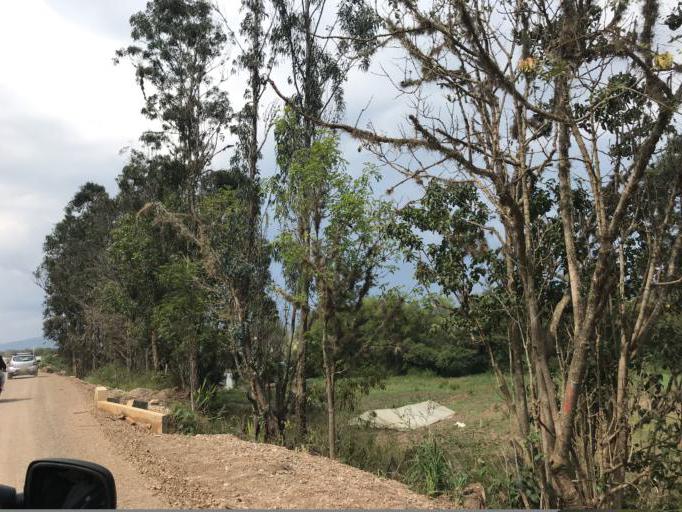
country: CO
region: Boyaca
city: Villa de Leiva
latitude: 5.6483
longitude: -73.5919
